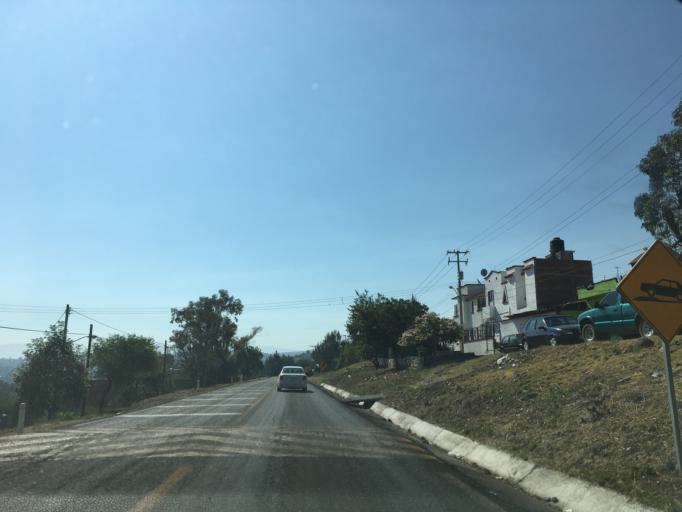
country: MX
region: Michoacan
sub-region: Morelia
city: Fraccionamiento Mision del Valle
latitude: 19.7378
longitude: -101.0963
